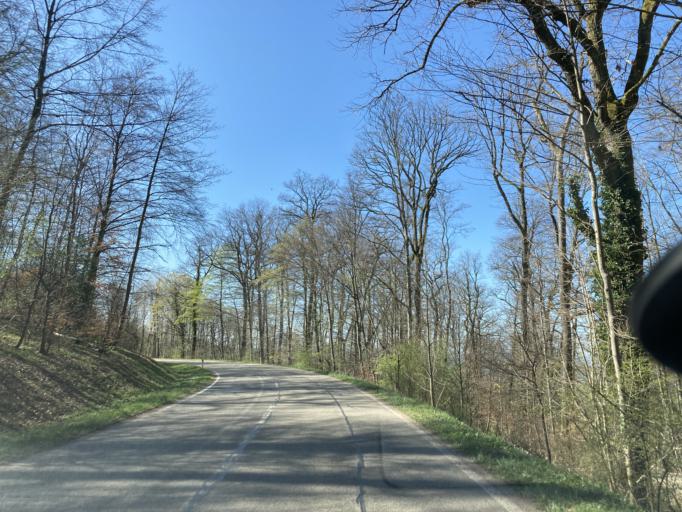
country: DE
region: Baden-Wuerttemberg
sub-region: Freiburg Region
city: Feldberg
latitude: 47.7746
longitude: 7.6640
